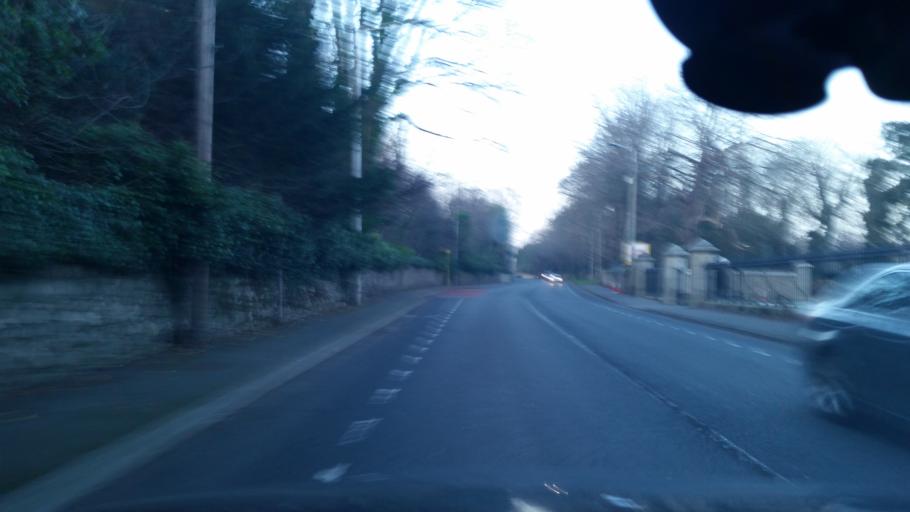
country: IE
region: Leinster
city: Shankill
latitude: 53.2192
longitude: -6.1202
